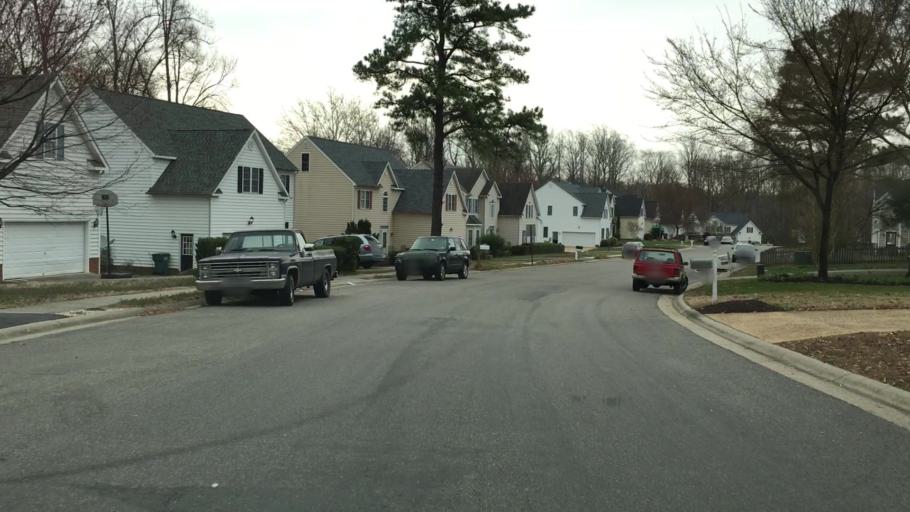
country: US
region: Virginia
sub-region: Henrico County
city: Short Pump
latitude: 37.6517
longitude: -77.5698
